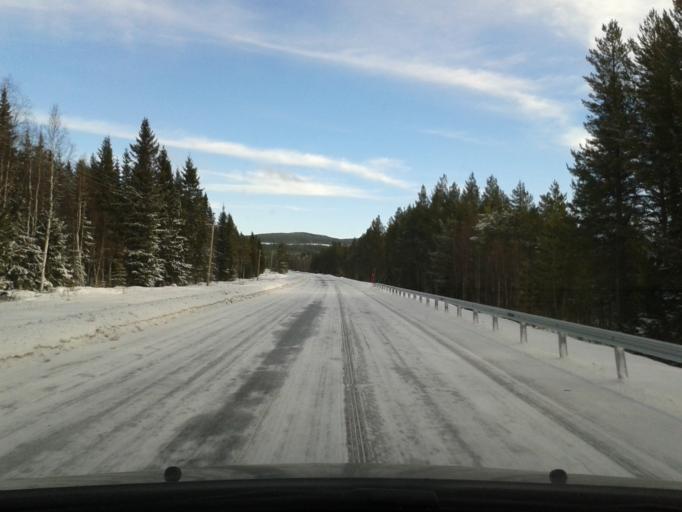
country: SE
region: Vaesterbotten
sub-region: Asele Kommun
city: Asele
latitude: 64.3413
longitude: 17.0199
